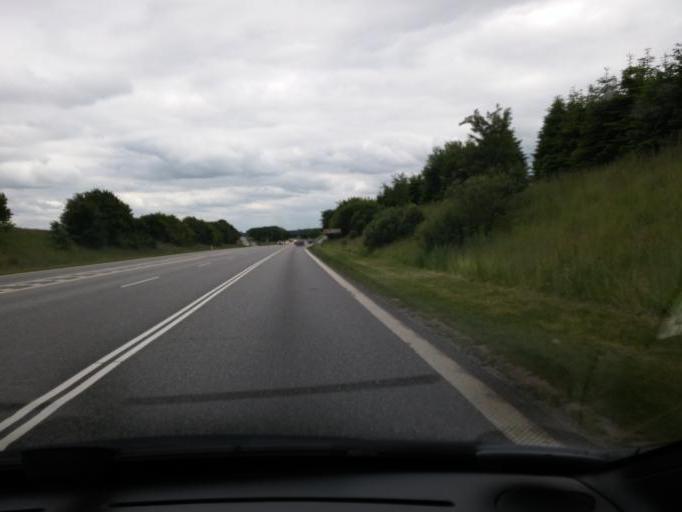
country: DK
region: Capital Region
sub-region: Hillerod Kommune
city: Hillerod
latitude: 55.9124
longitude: 12.2655
